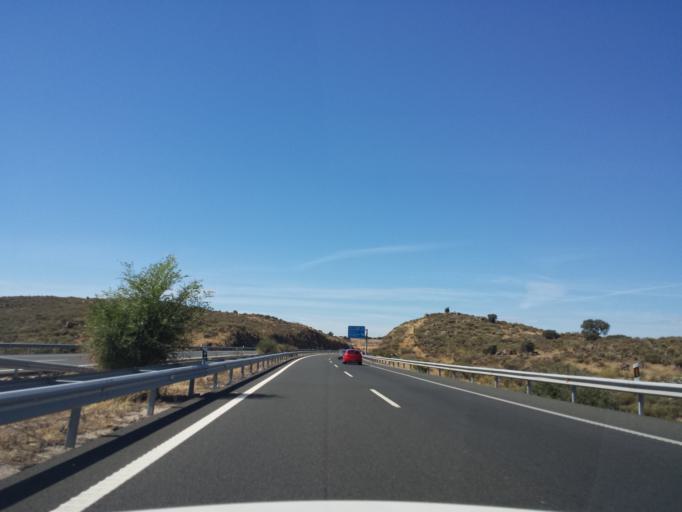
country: ES
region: Extremadura
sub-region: Provincia de Caceres
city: Navalmoral de la Mata
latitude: 39.8809
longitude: -5.5380
